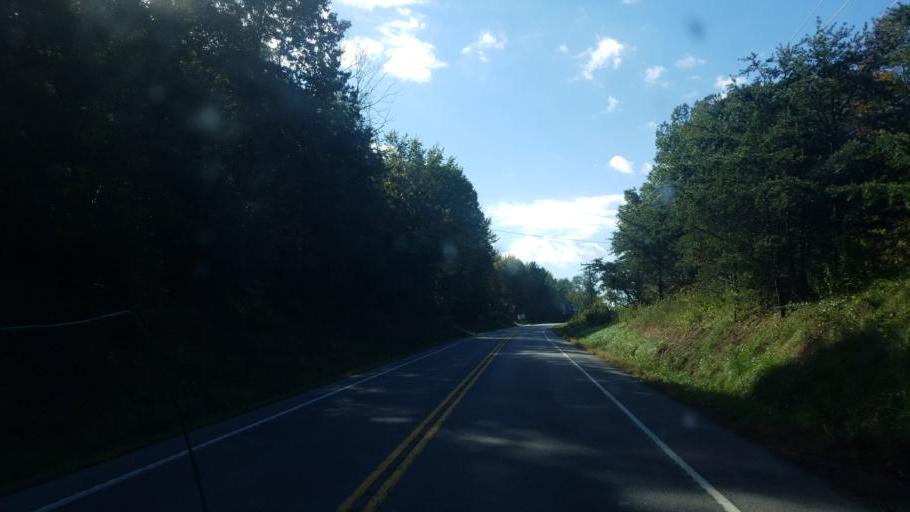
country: US
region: Pennsylvania
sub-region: Bedford County
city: Bedford
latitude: 40.1495
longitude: -78.5118
